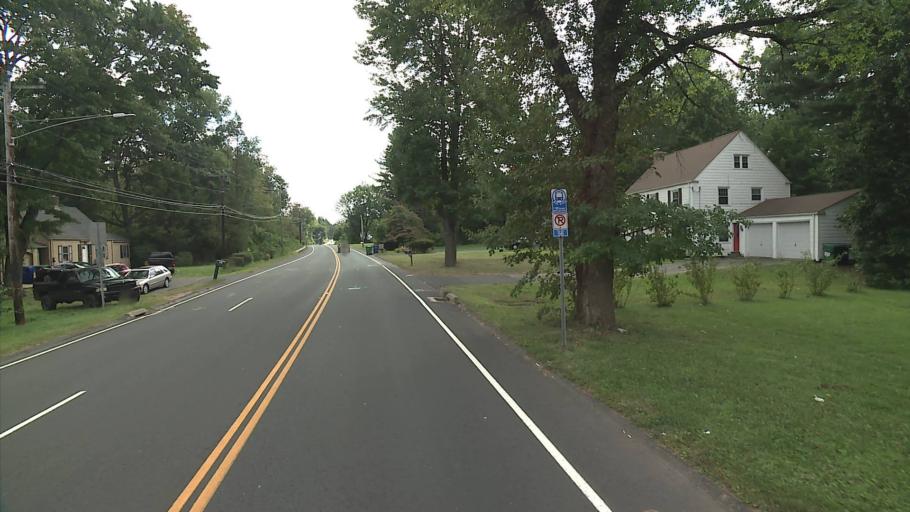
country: US
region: Connecticut
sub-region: Hartford County
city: Blue Hills
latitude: 41.8150
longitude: -72.7376
